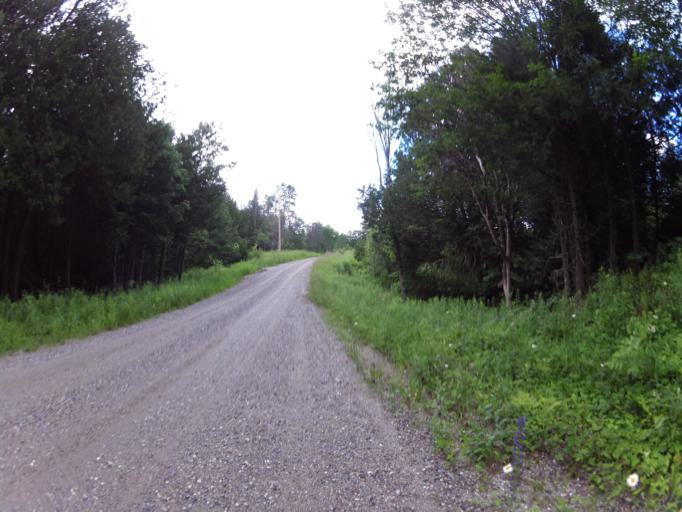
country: CA
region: Ontario
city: Renfrew
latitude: 45.0627
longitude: -76.7552
